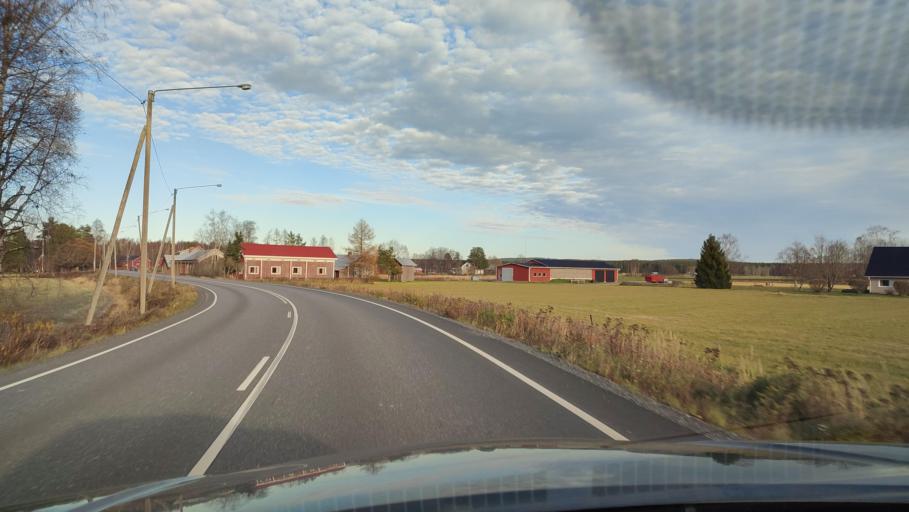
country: FI
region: Ostrobothnia
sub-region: Sydosterbotten
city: Kristinestad
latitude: 62.2635
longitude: 21.5399
